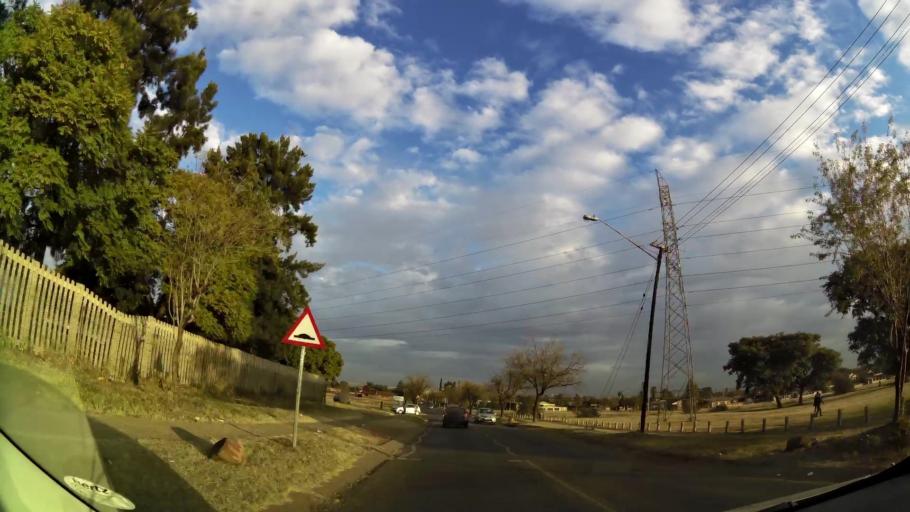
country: ZA
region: Gauteng
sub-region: City of Tshwane Metropolitan Municipality
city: Pretoria
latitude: -25.7117
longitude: 28.3204
